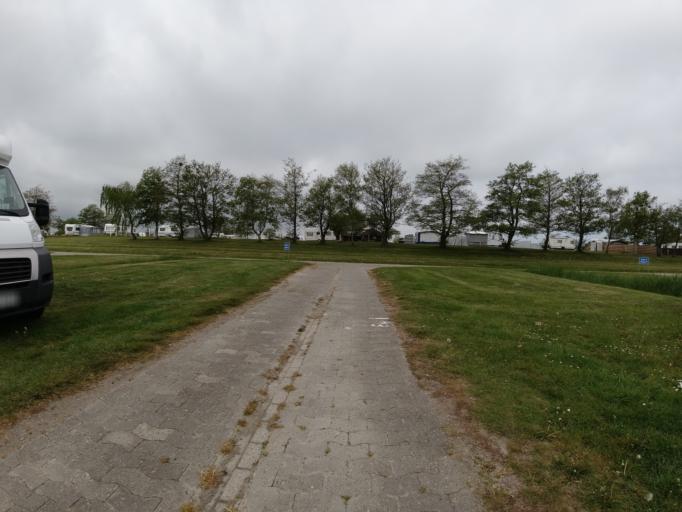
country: DE
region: Lower Saxony
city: Schillig
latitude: 53.6976
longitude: 8.0247
